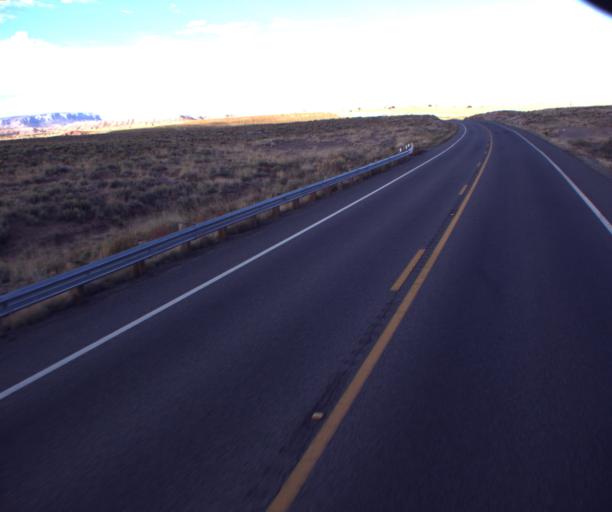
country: US
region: New Mexico
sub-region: San Juan County
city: Shiprock
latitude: 36.9363
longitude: -109.1180
